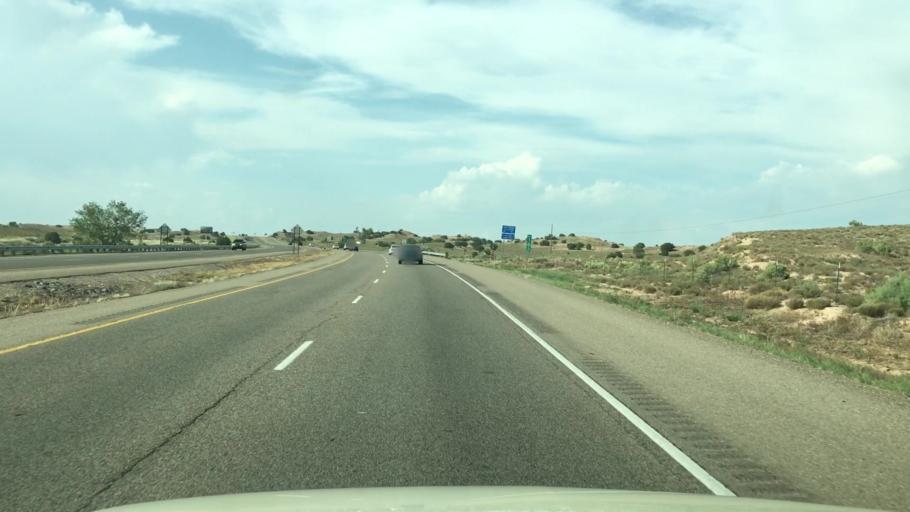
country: US
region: New Mexico
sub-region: Santa Fe County
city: Pojoaque
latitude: 35.9137
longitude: -106.0165
